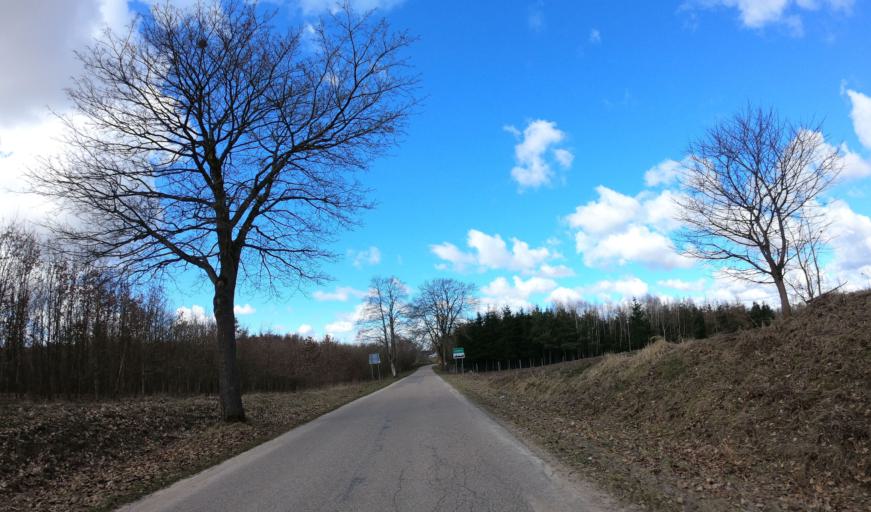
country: PL
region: West Pomeranian Voivodeship
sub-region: Powiat drawski
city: Zlocieniec
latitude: 53.4828
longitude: 15.9155
